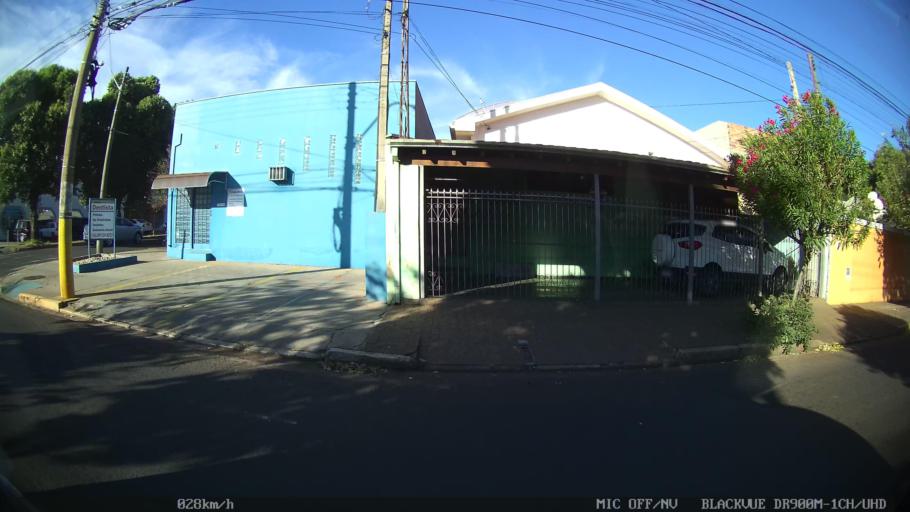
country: BR
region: Sao Paulo
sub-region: Araraquara
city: Araraquara
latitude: -21.7603
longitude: -48.1634
